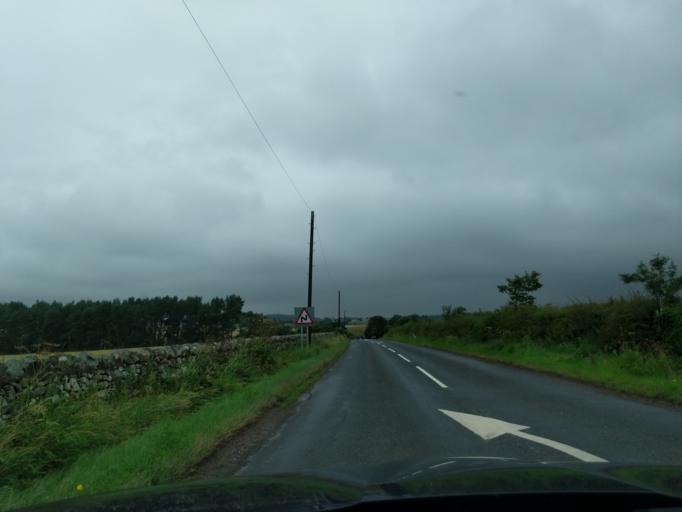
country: GB
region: England
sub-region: Northumberland
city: Ford
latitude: 55.6615
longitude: -2.1058
